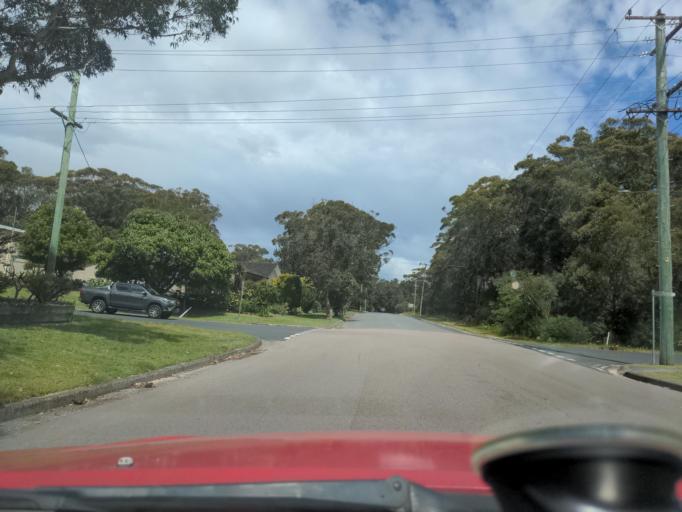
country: AU
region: New South Wales
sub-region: Great Lakes
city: Hawks Nest
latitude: -32.6746
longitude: 152.1769
